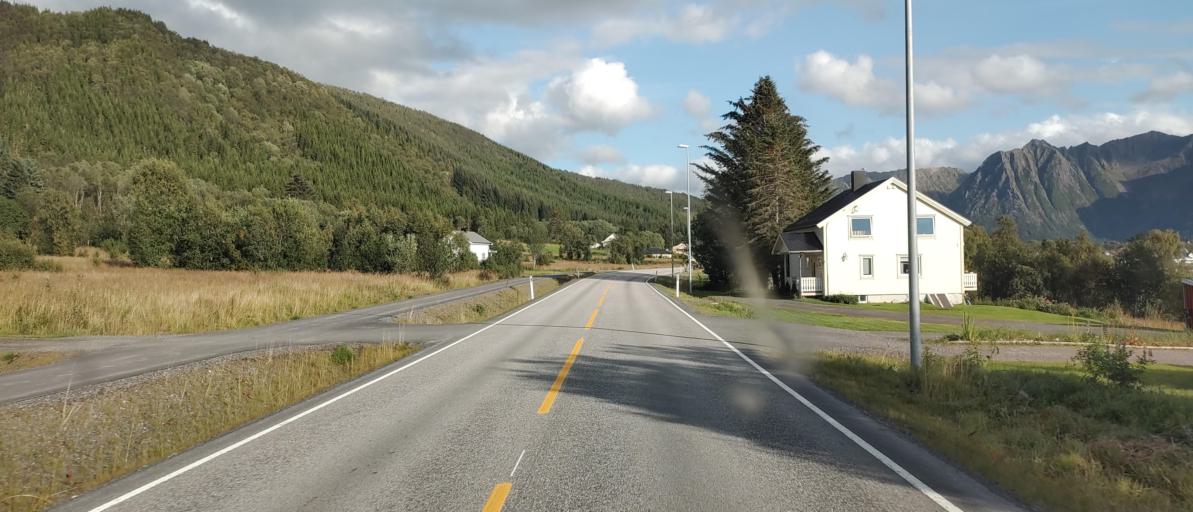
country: NO
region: Nordland
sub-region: Sortland
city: Sortland
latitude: 68.7509
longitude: 15.4872
